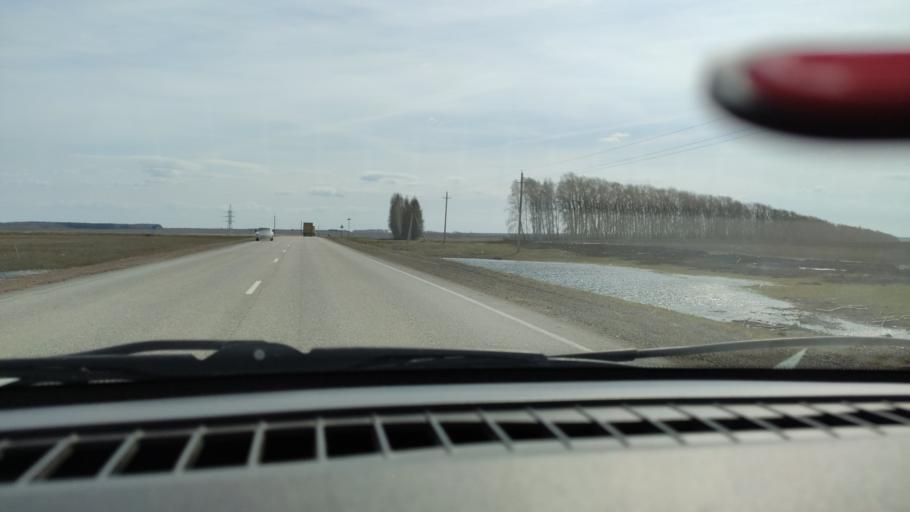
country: RU
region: Bashkortostan
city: Dyurtyuli
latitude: 55.3356
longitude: 54.9527
